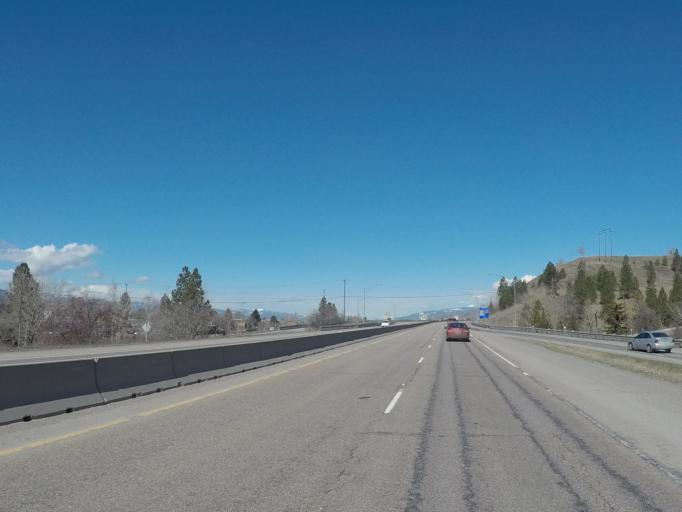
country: US
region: Montana
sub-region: Missoula County
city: Missoula
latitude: 46.8714
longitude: -113.9824
